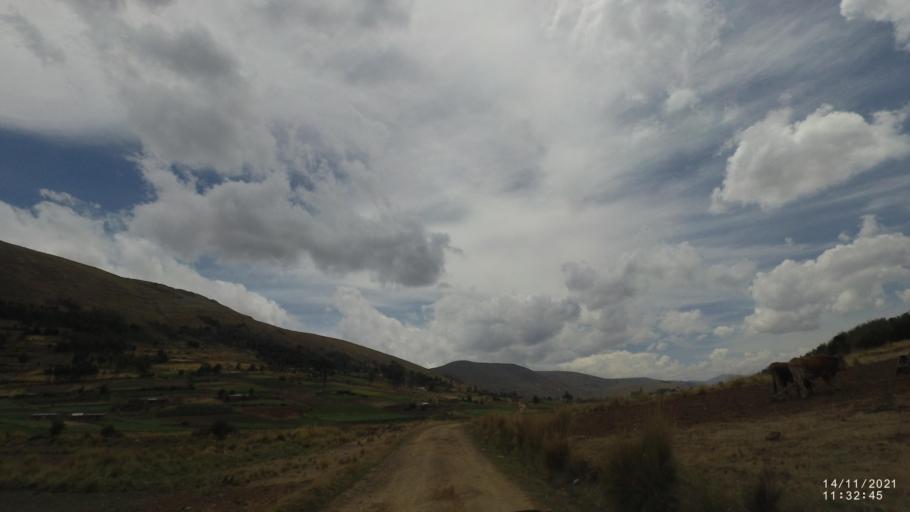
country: BO
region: Cochabamba
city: Colomi
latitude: -17.3442
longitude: -66.0096
